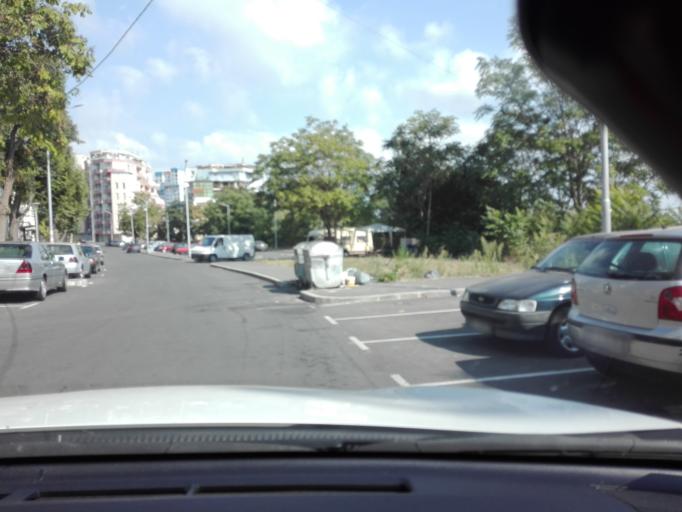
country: BG
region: Burgas
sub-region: Obshtina Burgas
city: Burgas
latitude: 42.4578
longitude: 27.4237
